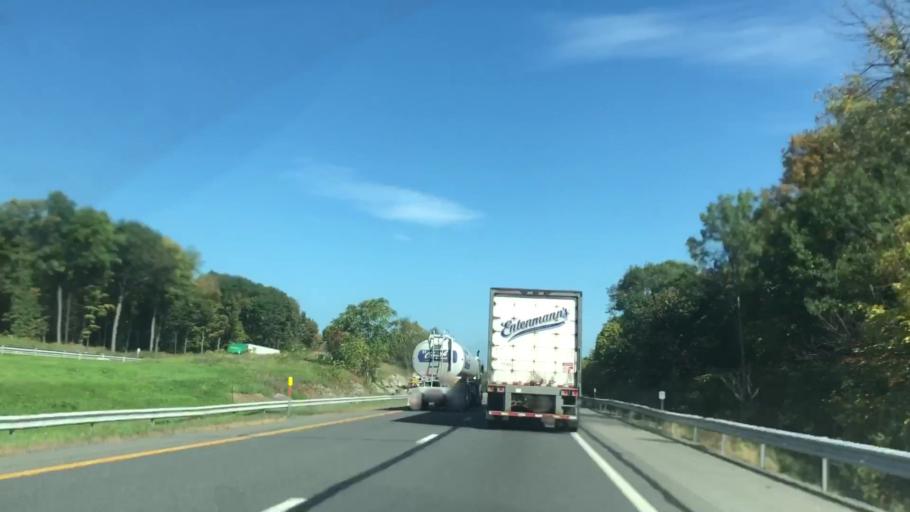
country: US
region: New York
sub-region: Greene County
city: Coxsackie
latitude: 42.3448
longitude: -73.8566
